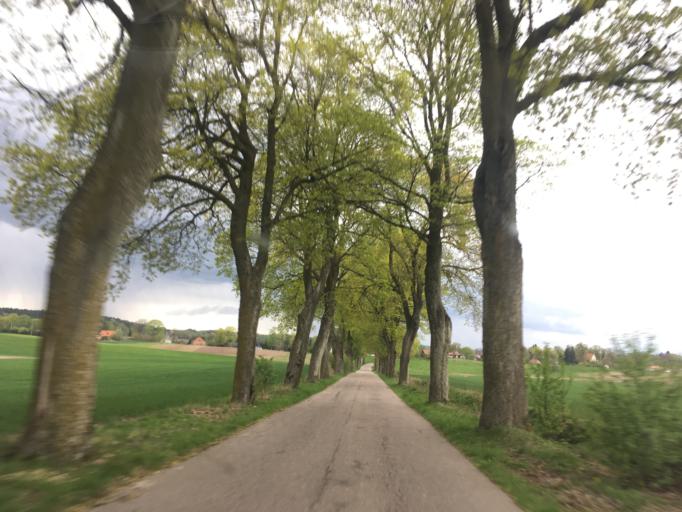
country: PL
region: Warmian-Masurian Voivodeship
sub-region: Powiat ostrodzki
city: Dabrowno
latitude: 53.4168
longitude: 20.0831
